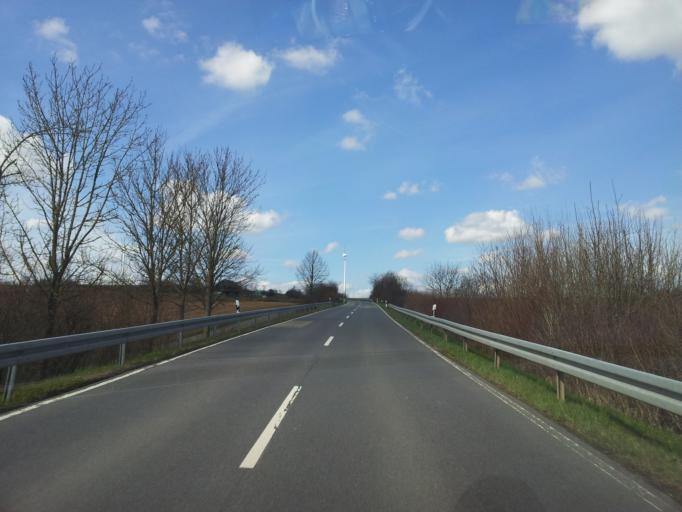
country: DE
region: Baden-Wuerttemberg
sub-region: Regierungsbezirk Stuttgart
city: Grossrinderfeld
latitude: 49.7019
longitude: 9.7784
